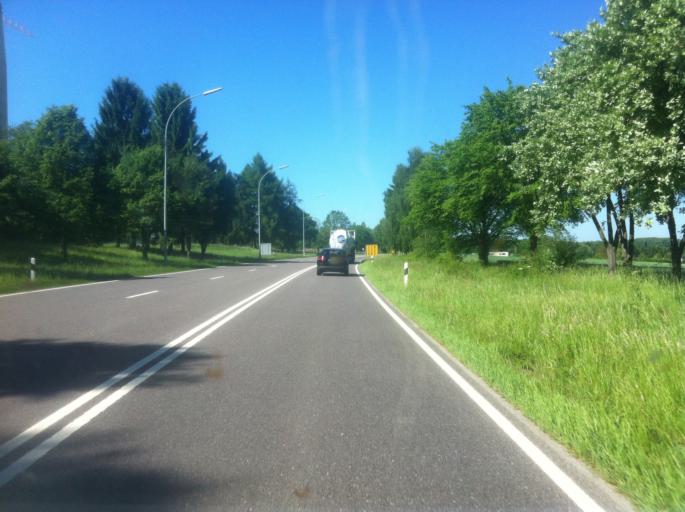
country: LU
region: Grevenmacher
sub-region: Canton d'Echternach
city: Consdorf
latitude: 49.7543
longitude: 6.3354
